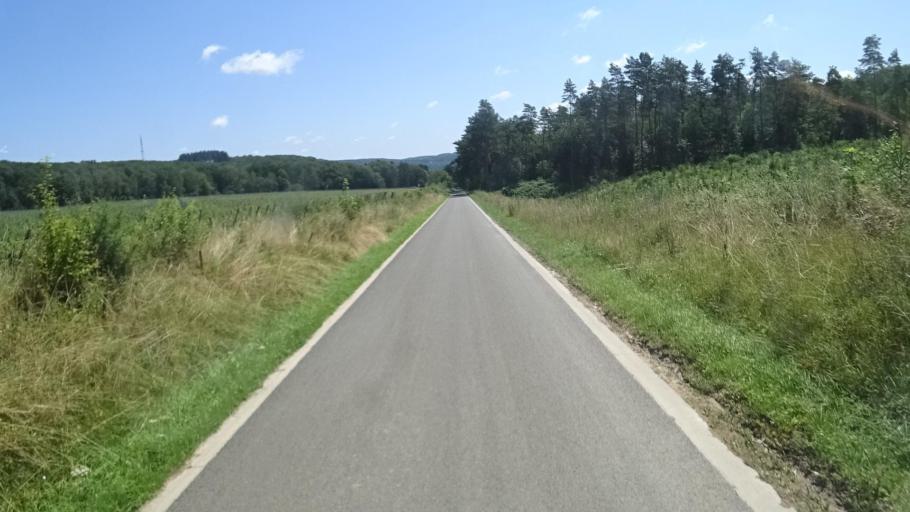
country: BE
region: Wallonia
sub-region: Province de Namur
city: Profondeville
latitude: 50.3546
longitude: 4.8294
